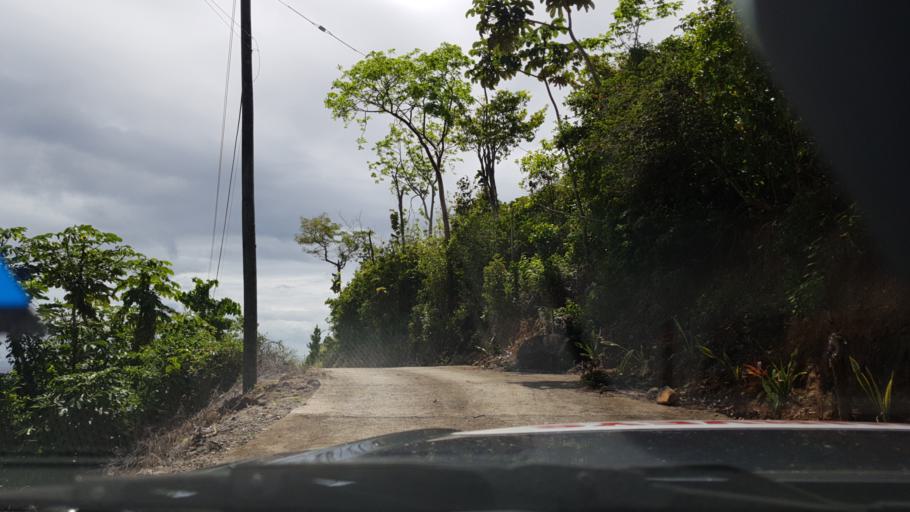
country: LC
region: Anse-la-Raye
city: Anse La Raye
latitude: 13.9436
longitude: -61.0346
